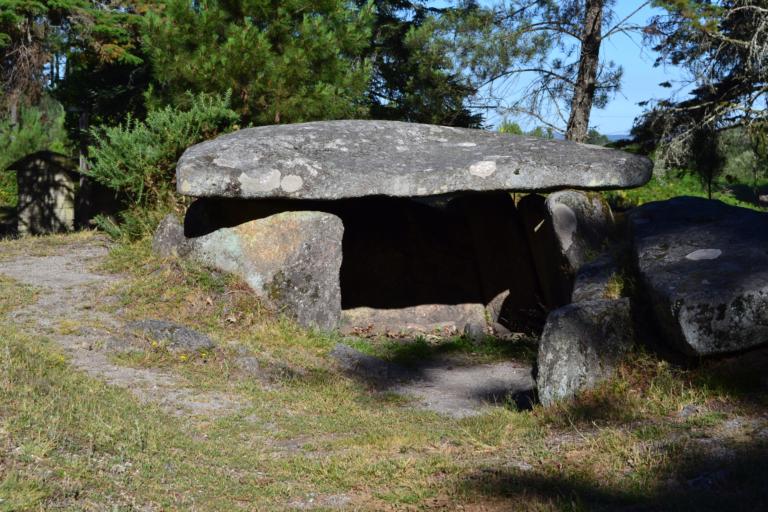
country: PT
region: Viana do Castelo
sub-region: Arcos de Valdevez
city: Mozelos
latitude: 41.8841
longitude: -8.3138
